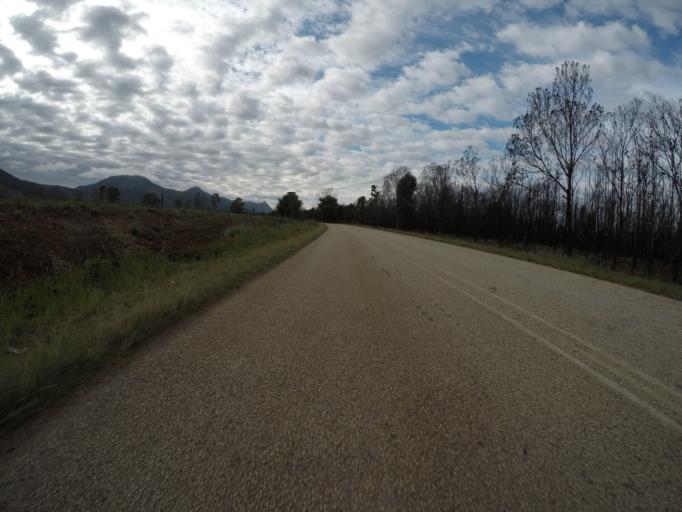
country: ZA
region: Eastern Cape
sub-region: Cacadu District Municipality
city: Kareedouw
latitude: -34.0142
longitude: 24.3173
